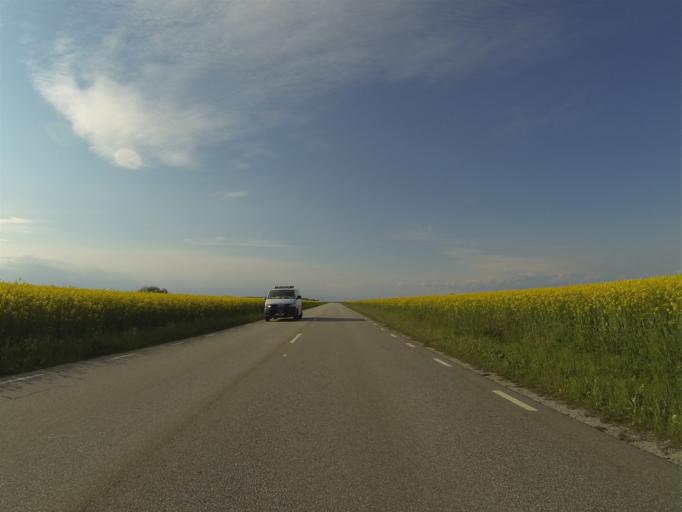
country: SE
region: Skane
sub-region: Lunds Kommun
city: Lund
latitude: 55.7015
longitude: 13.3045
